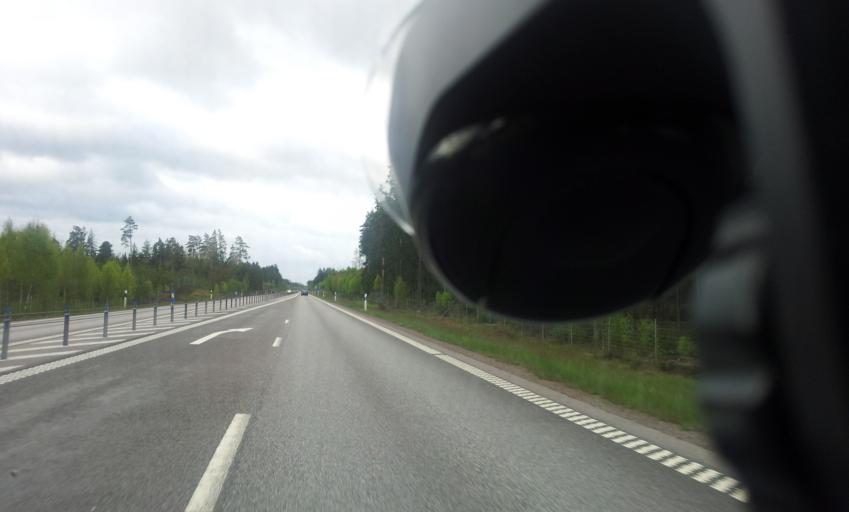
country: SE
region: Kalmar
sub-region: Kalmar Kommun
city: Ljungbyholm
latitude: 56.5299
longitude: 16.0842
